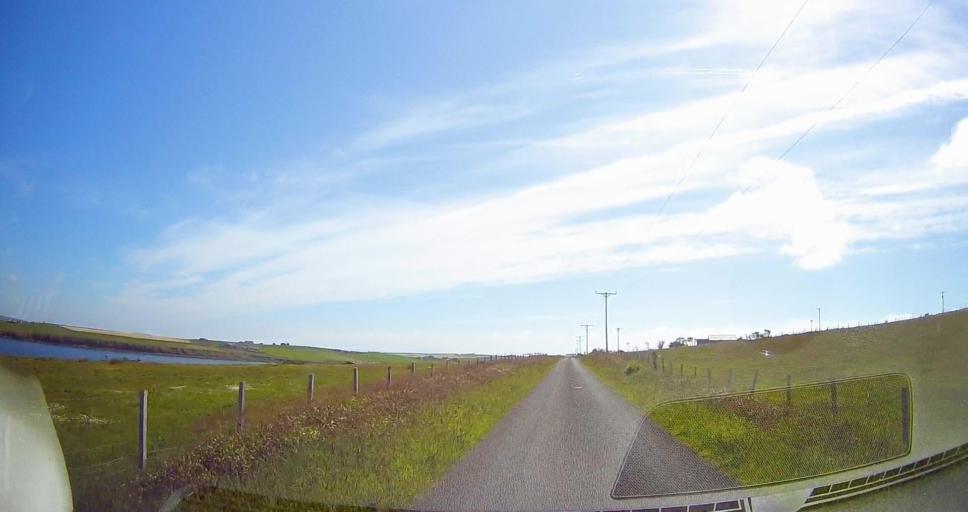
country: GB
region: Scotland
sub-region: Orkney Islands
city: Kirkwall
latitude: 58.8568
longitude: -2.9343
